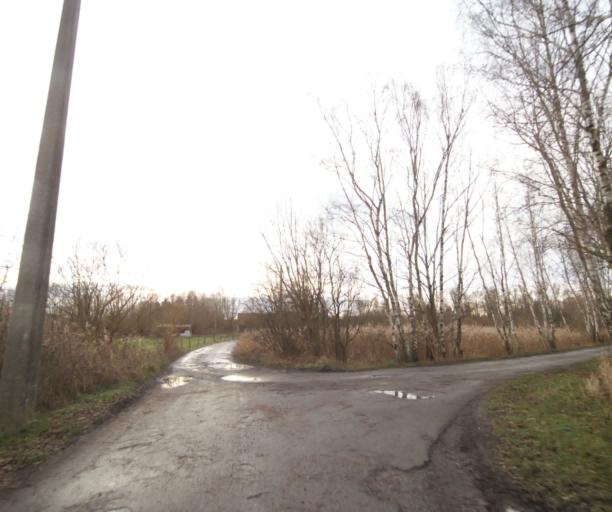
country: BE
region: Wallonia
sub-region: Province du Hainaut
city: Bernissart
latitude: 50.4582
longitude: 3.6268
